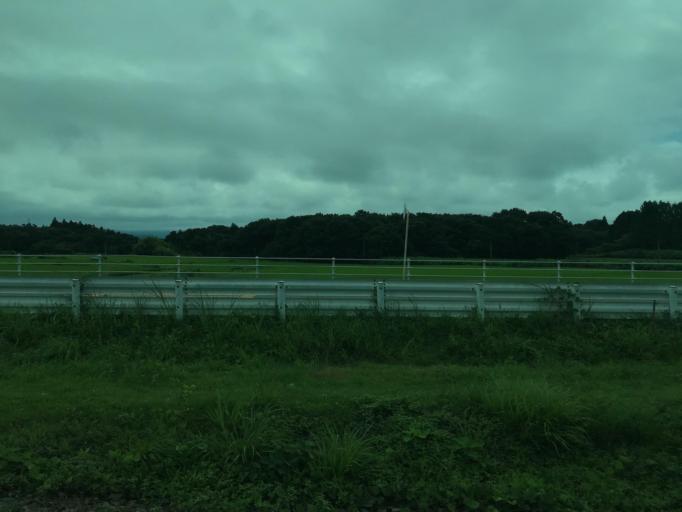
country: JP
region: Tochigi
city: Kuroiso
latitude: 37.0104
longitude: 140.0961
